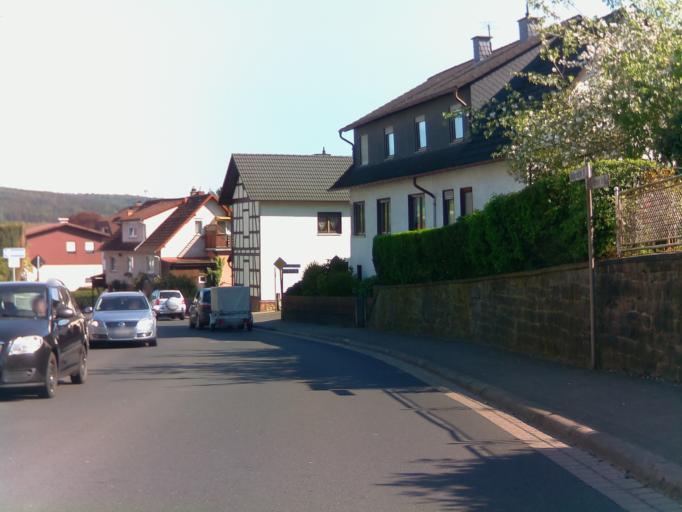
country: DE
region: Hesse
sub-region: Regierungsbezirk Darmstadt
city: Birstein
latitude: 50.3070
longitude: 9.2949
